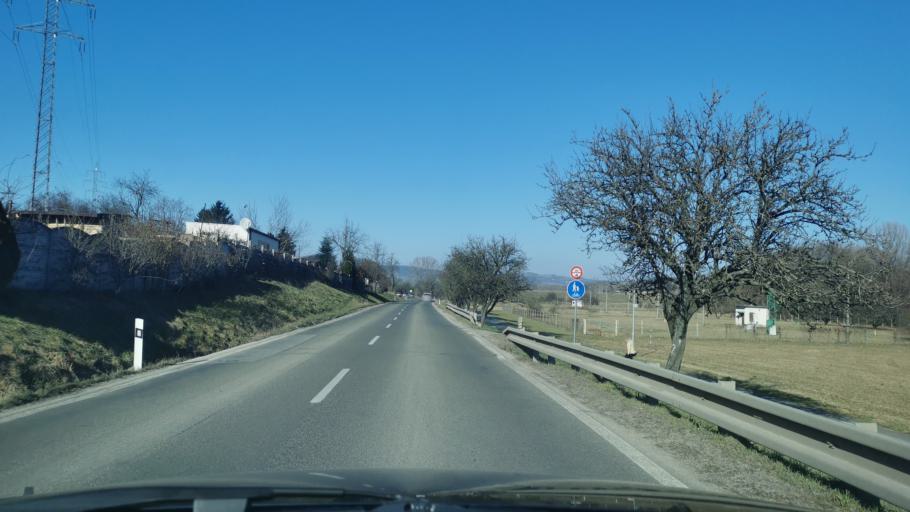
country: SK
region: Trnavsky
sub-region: Okres Senica
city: Senica
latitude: 48.6969
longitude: 17.3997
